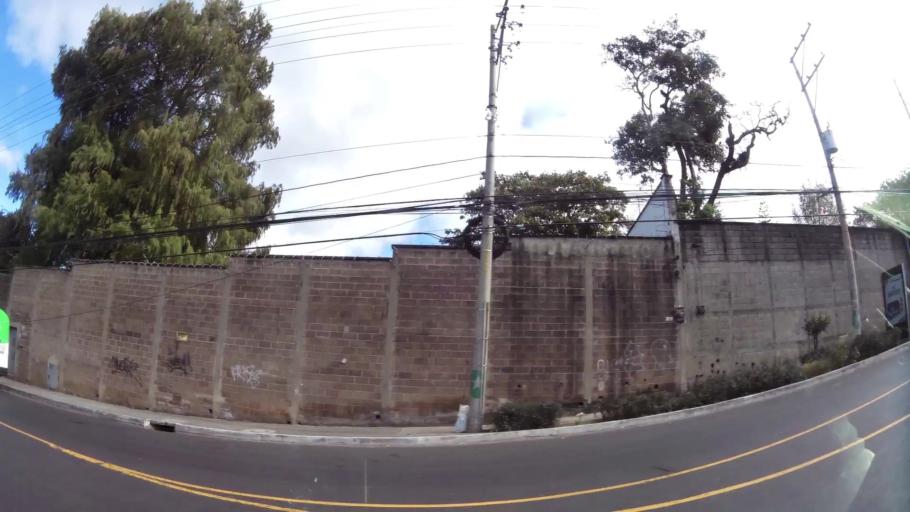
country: GT
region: Guatemala
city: Santa Catarina Pinula
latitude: 14.5775
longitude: -90.4926
